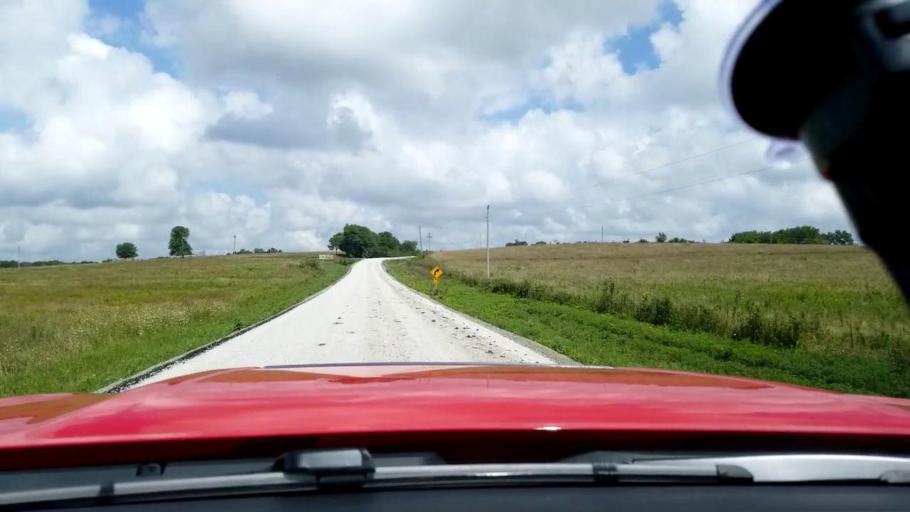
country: US
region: Iowa
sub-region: Decatur County
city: Lamoni
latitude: 40.6506
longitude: -94.0530
